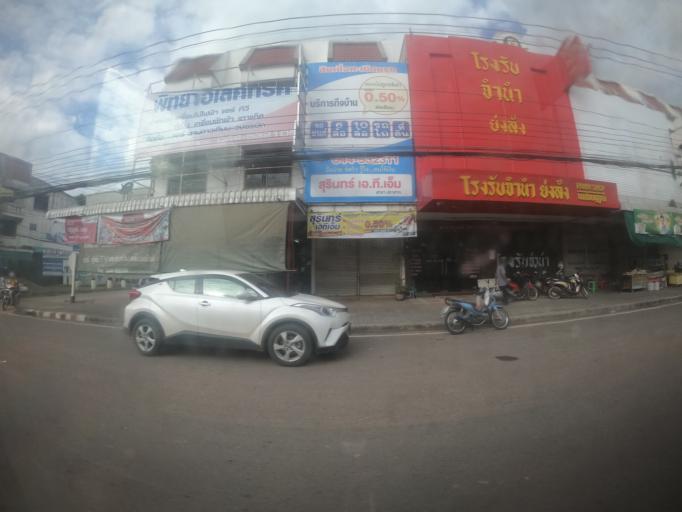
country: TH
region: Surin
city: Prasat
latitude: 14.6333
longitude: 103.4078
